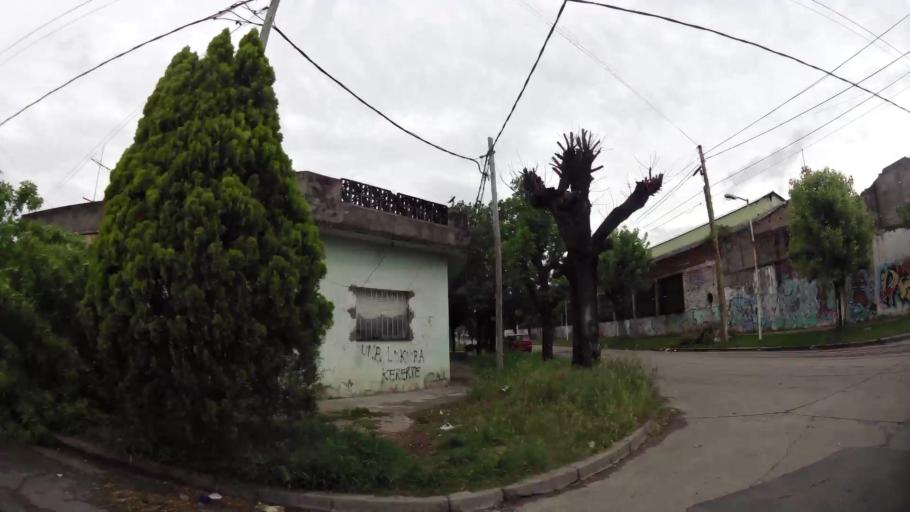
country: AR
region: Buenos Aires
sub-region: Partido de Lanus
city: Lanus
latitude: -34.7288
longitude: -58.3648
